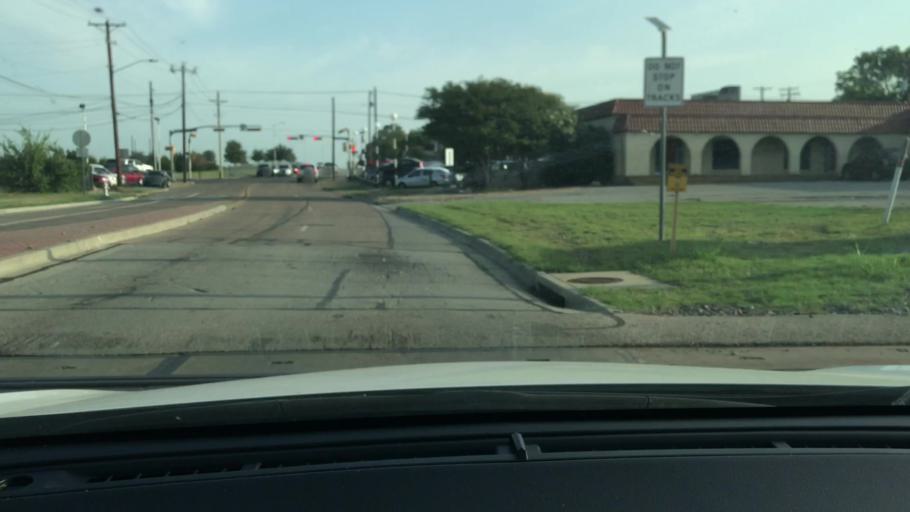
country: US
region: Texas
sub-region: Tarrant County
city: Arlington
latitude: 32.7379
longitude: -97.1232
